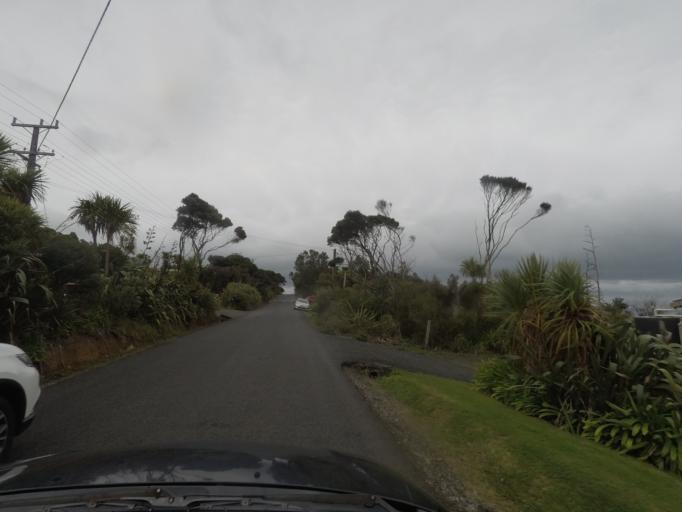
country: NZ
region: Auckland
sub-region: Auckland
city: Muriwai Beach
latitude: -36.9686
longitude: 174.4763
